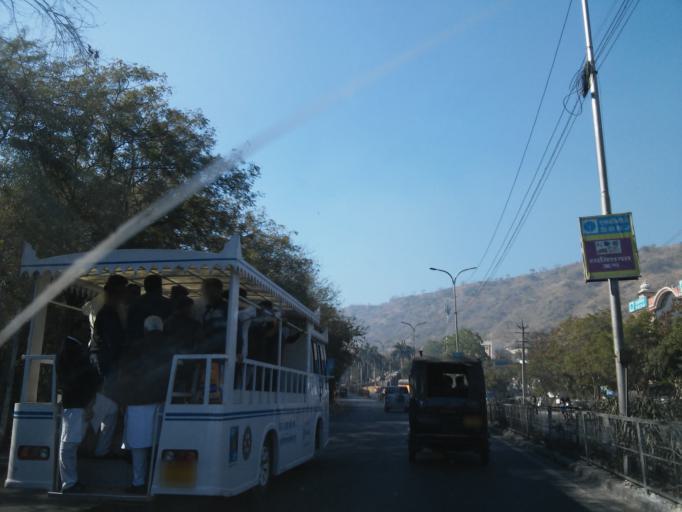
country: IN
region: Rajasthan
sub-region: Udaipur
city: Udaipur
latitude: 24.5662
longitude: 73.6947
